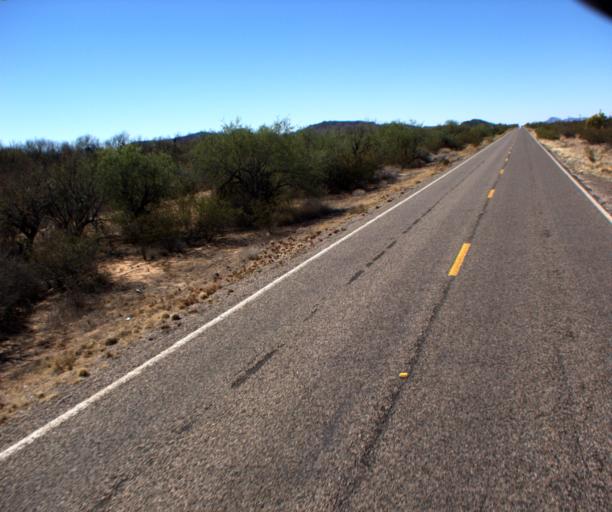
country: US
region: Arizona
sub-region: Pima County
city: Ajo
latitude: 32.2548
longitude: -112.7440
